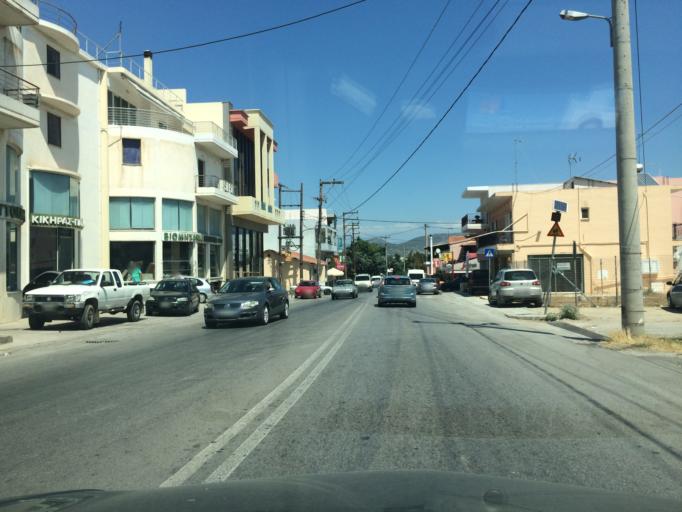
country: GR
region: Central Greece
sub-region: Nomos Evvoias
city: Chalkida
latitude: 38.4616
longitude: 23.6121
